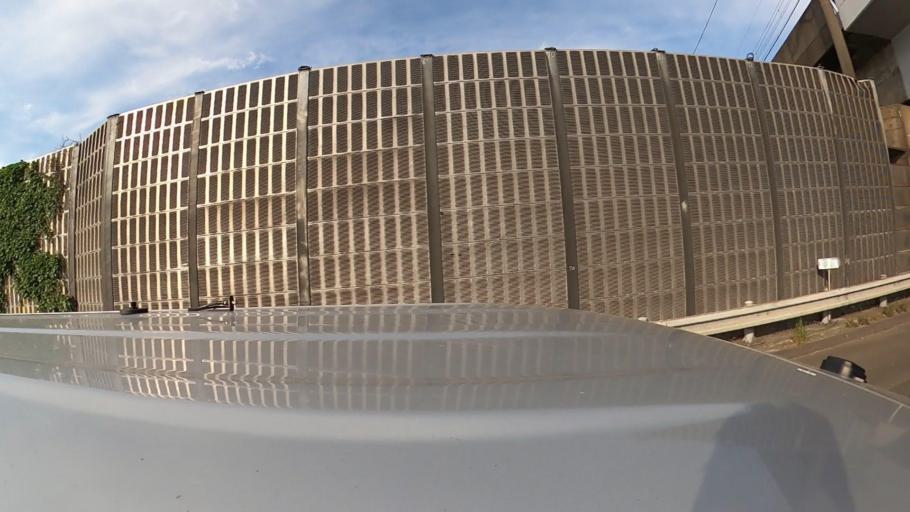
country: JP
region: Saitama
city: Oi
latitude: 35.8006
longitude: 139.5391
